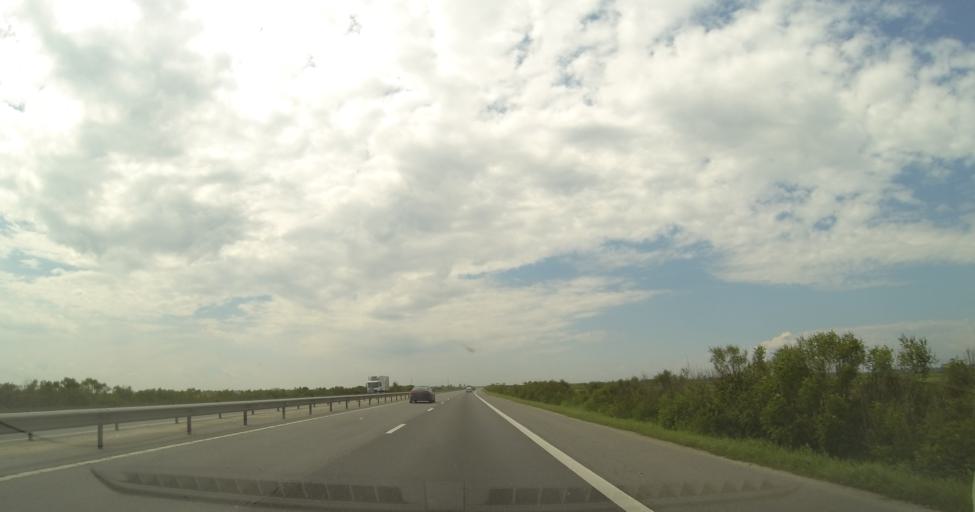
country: RO
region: Dambovita
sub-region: Comuna Petresti
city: Greci
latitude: 44.6499
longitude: 25.3641
